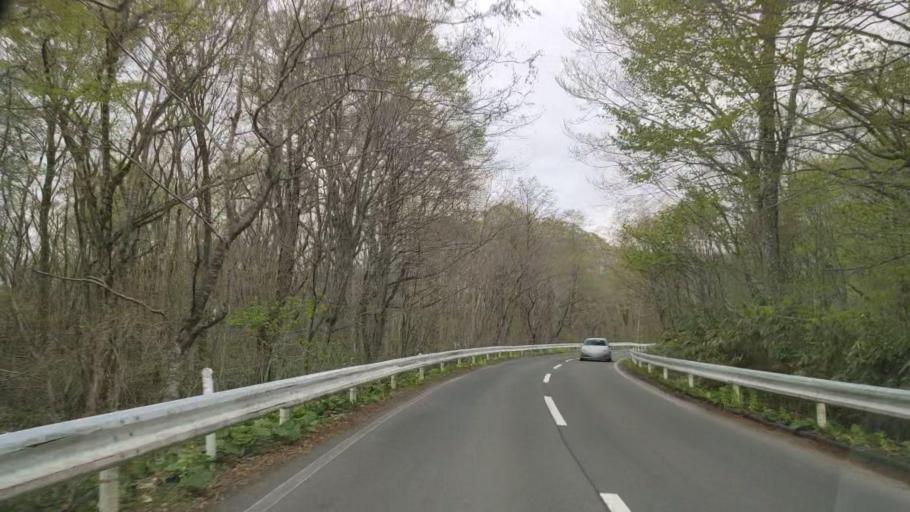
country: JP
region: Akita
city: Hanawa
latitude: 40.4020
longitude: 140.8059
